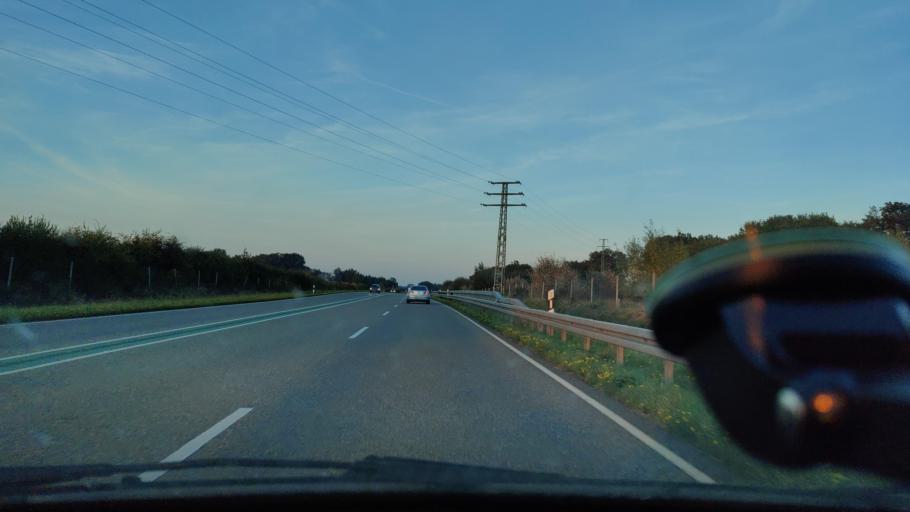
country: DE
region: North Rhine-Westphalia
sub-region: Regierungsbezirk Munster
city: Borken
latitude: 51.8215
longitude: 6.7858
